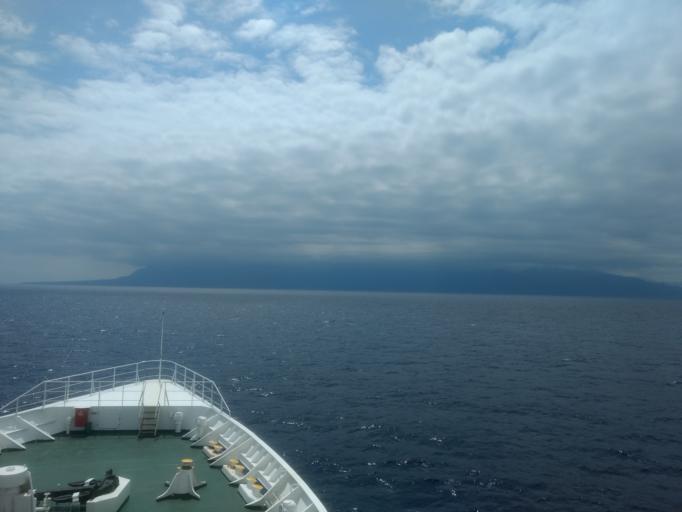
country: JP
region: Kagoshima
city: Nishinoomote
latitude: 30.5473
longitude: 130.6172
